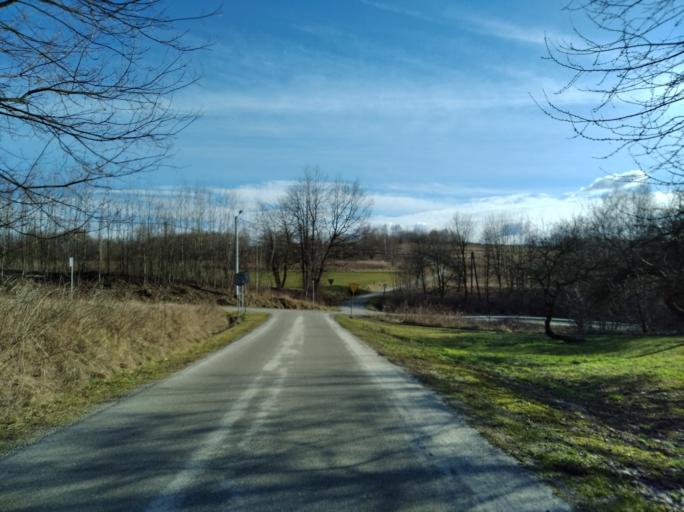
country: PL
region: Subcarpathian Voivodeship
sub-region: Powiat strzyzowski
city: Wisniowa
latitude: 49.8977
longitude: 21.6675
